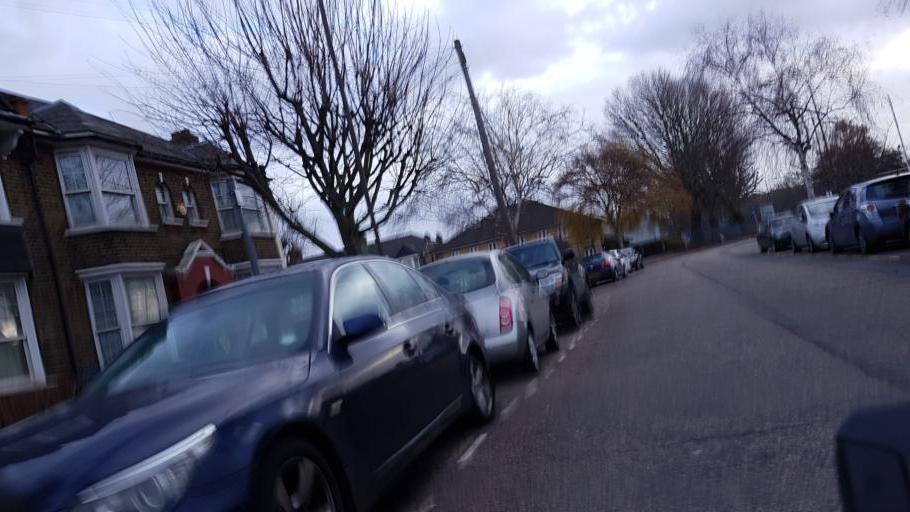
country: GB
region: England
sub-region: Greater London
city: Blackheath
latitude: 51.4917
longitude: 0.0299
